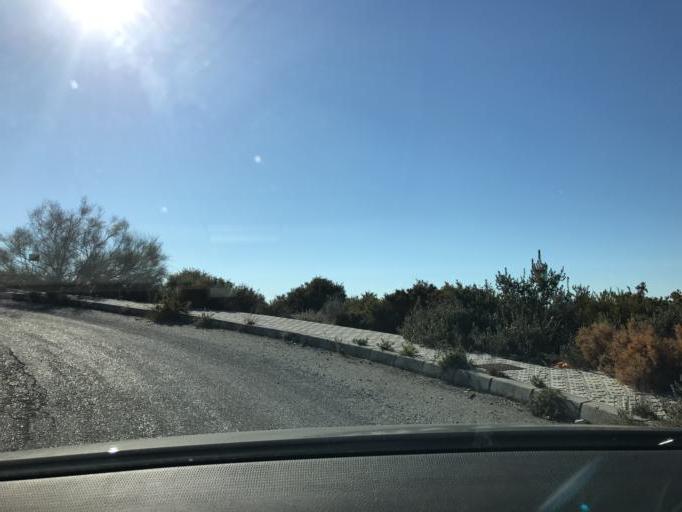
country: ES
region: Andalusia
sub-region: Provincia de Granada
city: Viznar
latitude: 37.2174
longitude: -3.5411
